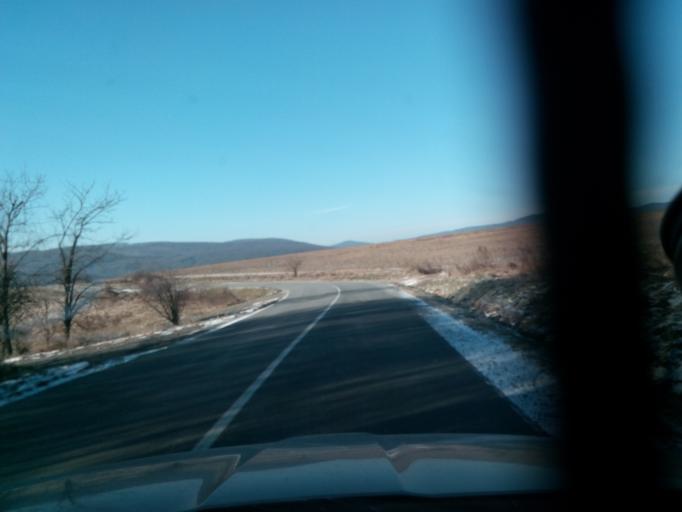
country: SK
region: Kosicky
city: Kosice
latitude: 48.7087
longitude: 21.1684
